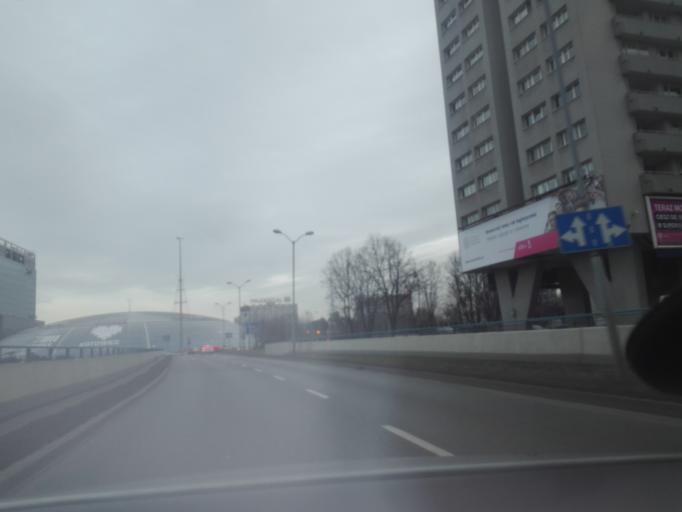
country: PL
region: Silesian Voivodeship
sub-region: Katowice
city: Katowice
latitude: 50.2646
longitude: 19.0210
